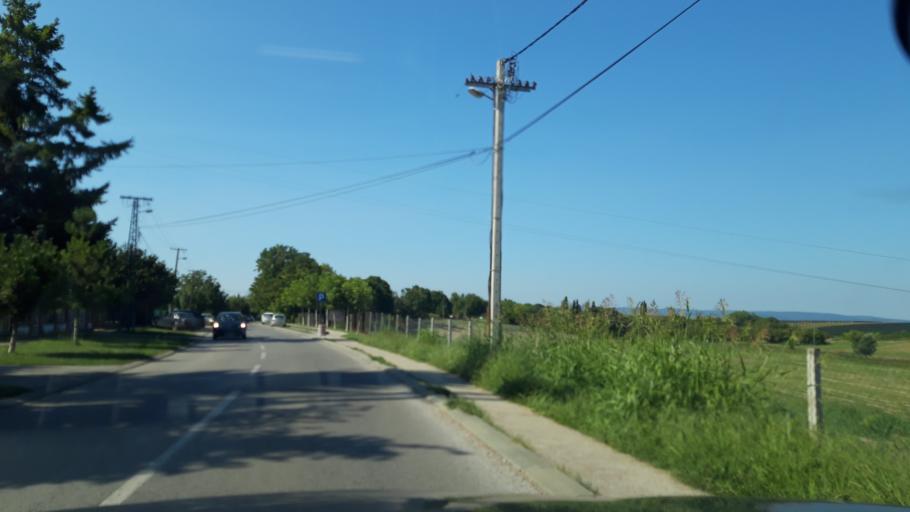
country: RS
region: Autonomna Pokrajina Vojvodina
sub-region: Sremski Okrug
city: Ruma
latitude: 45.0228
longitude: 19.8217
